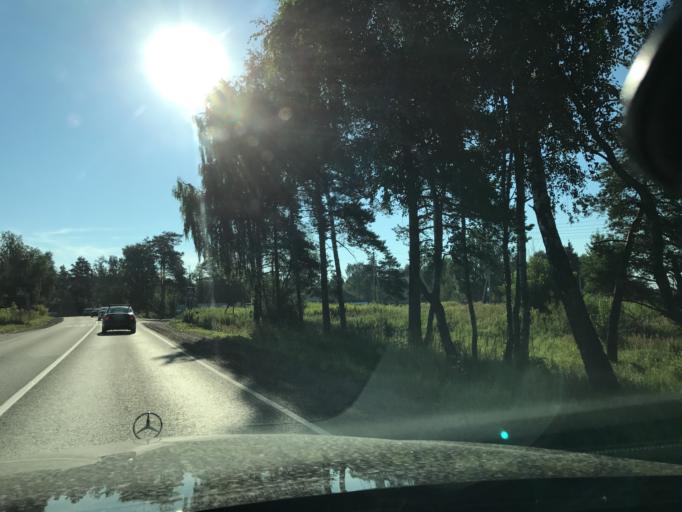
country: RU
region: Moskovskaya
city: Bakhchivandzhi
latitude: 55.8490
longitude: 38.1092
